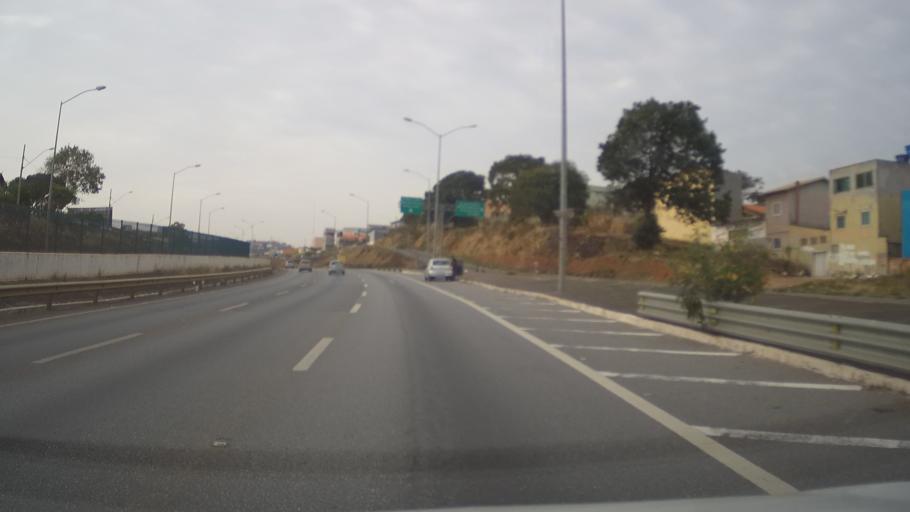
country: BR
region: Minas Gerais
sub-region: Vespasiano
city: Vespasiano
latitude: -19.7472
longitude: -43.9506
